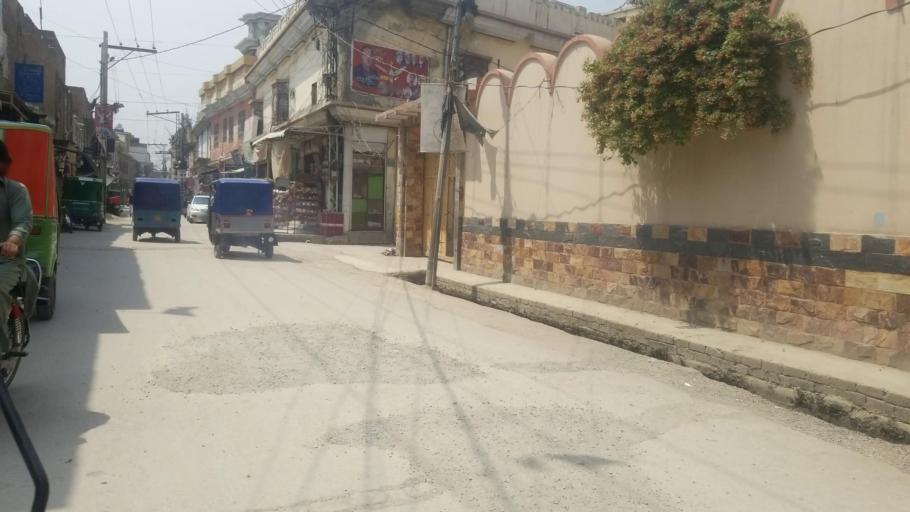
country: PK
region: Khyber Pakhtunkhwa
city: Peshawar
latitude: 34.0298
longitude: 71.5846
